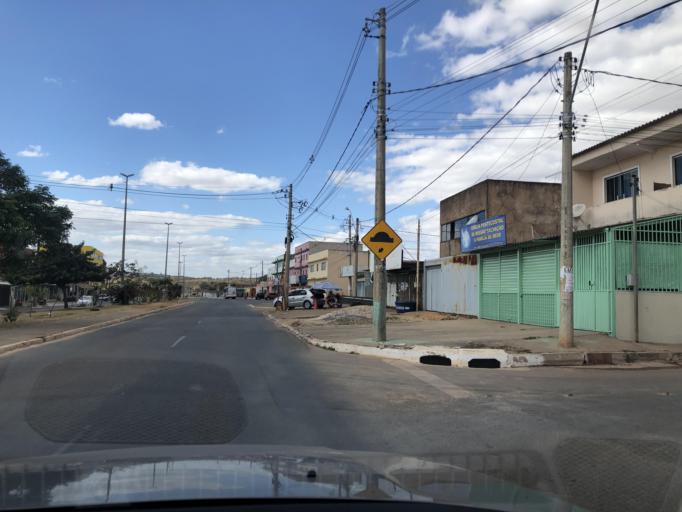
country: BR
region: Federal District
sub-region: Brasilia
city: Brasilia
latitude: -15.8868
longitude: -48.1470
